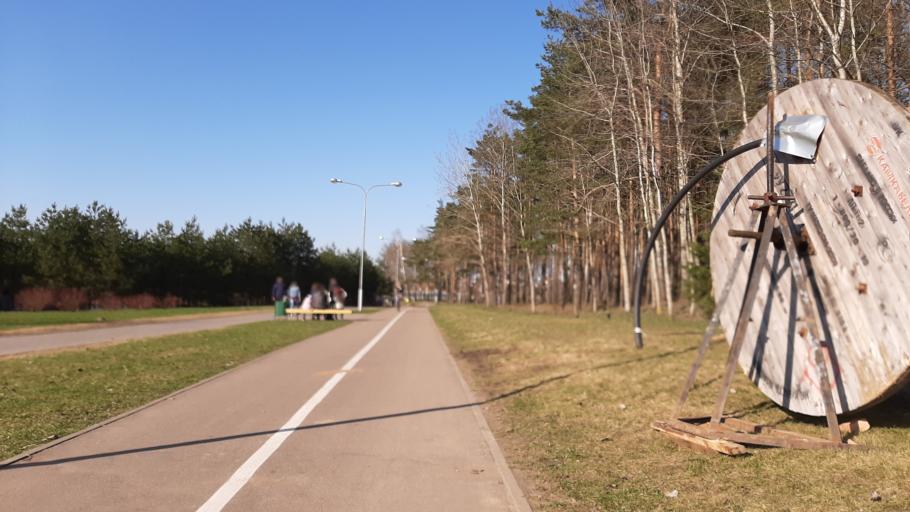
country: BY
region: Minsk
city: Bal'shavik
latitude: 53.9577
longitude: 27.5868
